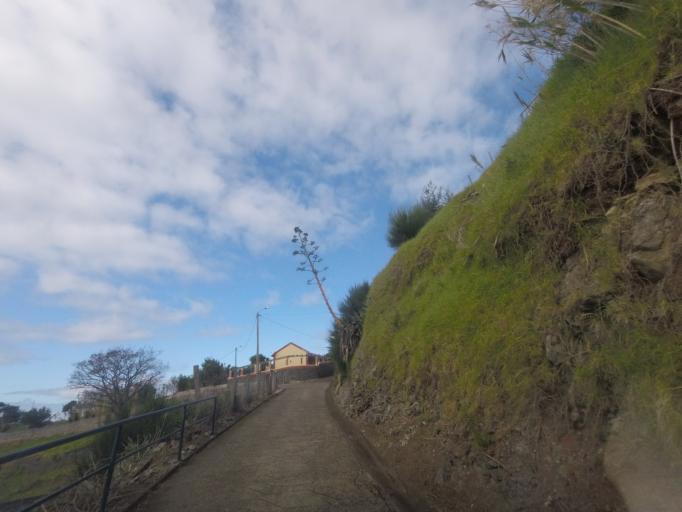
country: PT
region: Madeira
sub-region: Calheta
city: Faja da Ovelha
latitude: 32.8173
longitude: -17.2444
